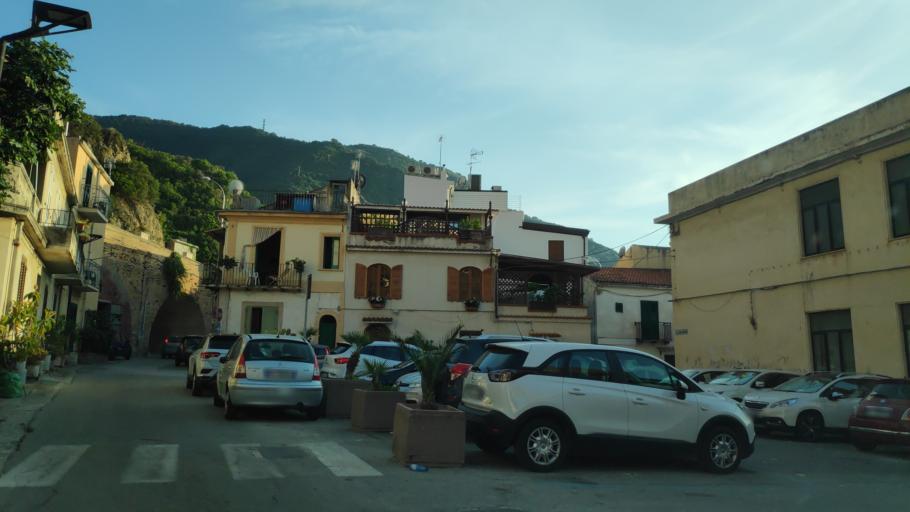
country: IT
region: Calabria
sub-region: Provincia di Reggio Calabria
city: Scilla
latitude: 38.2534
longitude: 15.7140
